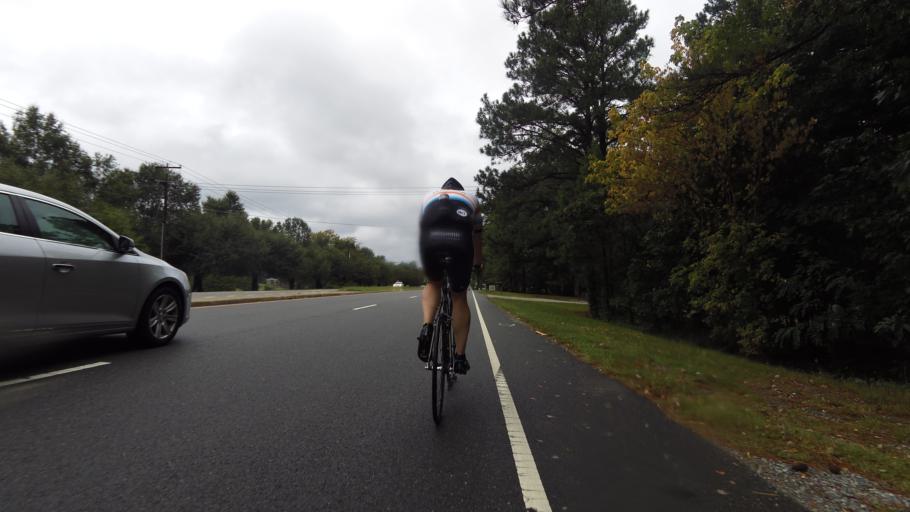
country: US
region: Virginia
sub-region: Henrico County
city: Short Pump
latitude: 37.5992
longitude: -77.6507
